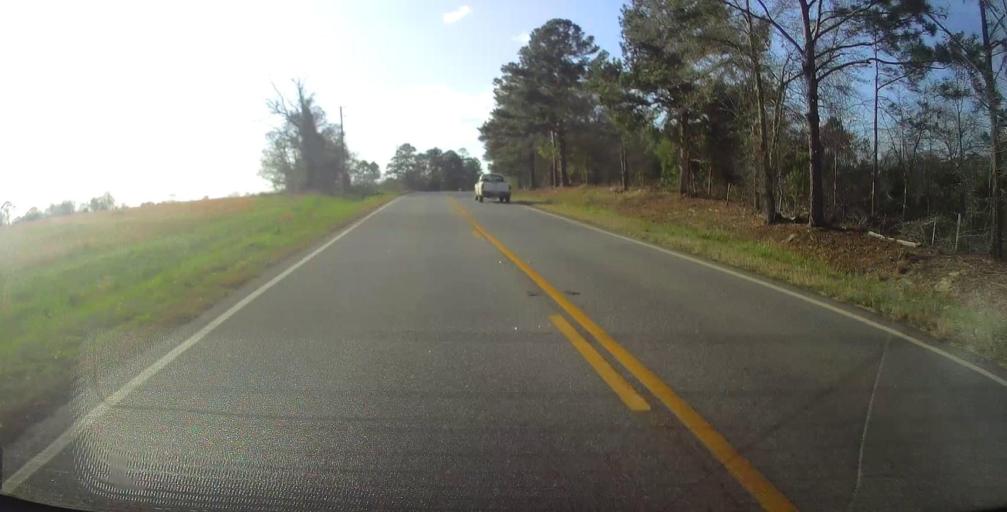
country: US
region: Georgia
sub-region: Toombs County
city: Lyons
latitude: 32.1440
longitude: -82.2546
